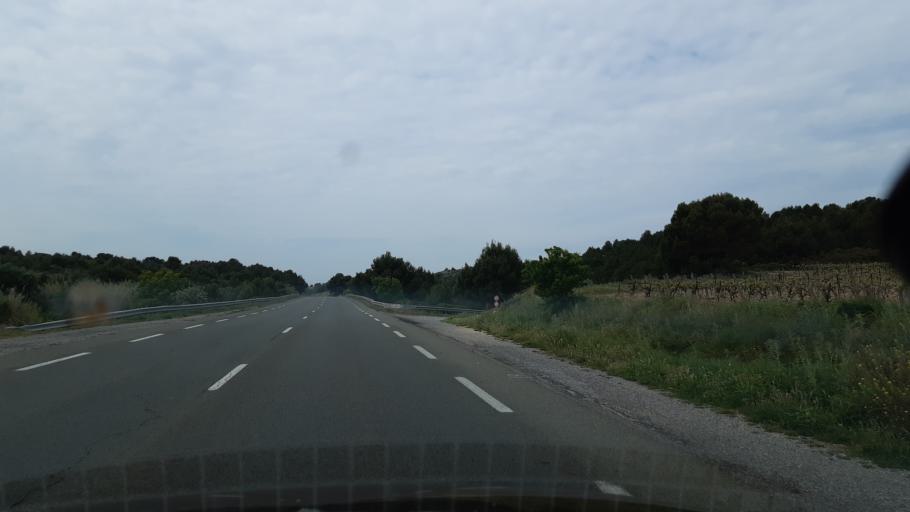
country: FR
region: Languedoc-Roussillon
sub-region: Departement de l'Aude
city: Gruissan
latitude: 43.1232
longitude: 3.0729
